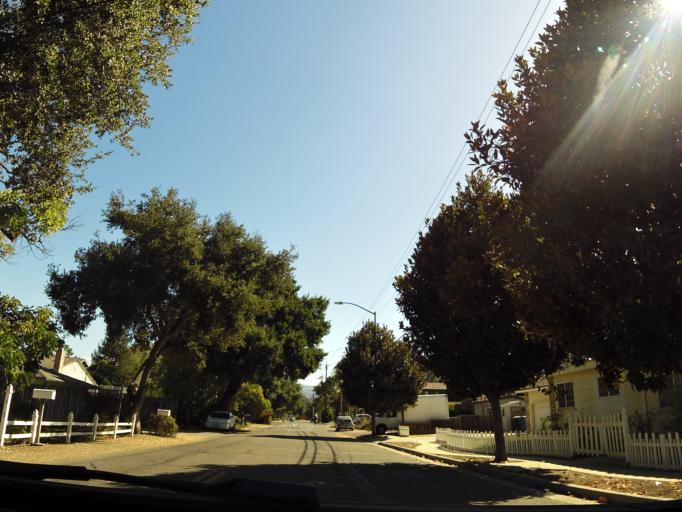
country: US
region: California
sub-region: Santa Clara County
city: Monte Sereno
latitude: 37.2682
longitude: -121.9802
